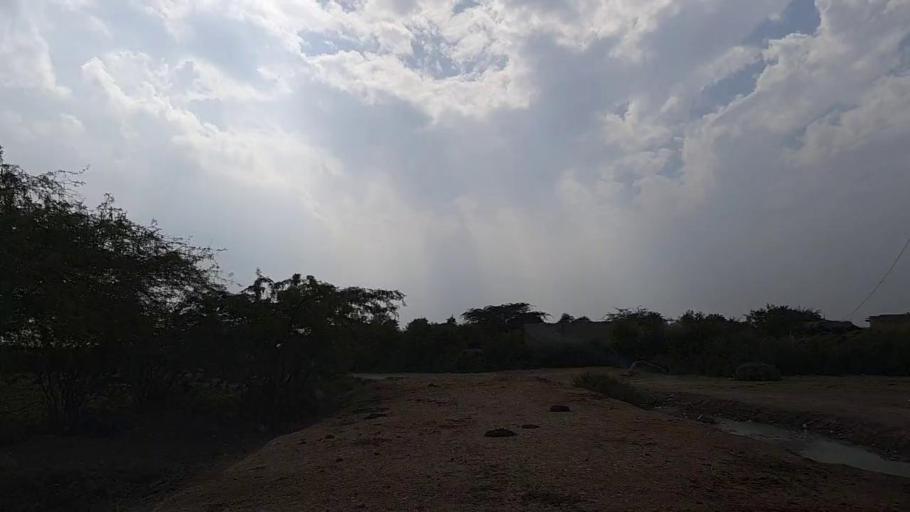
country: PK
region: Sindh
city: Daro Mehar
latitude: 24.7193
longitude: 68.1366
